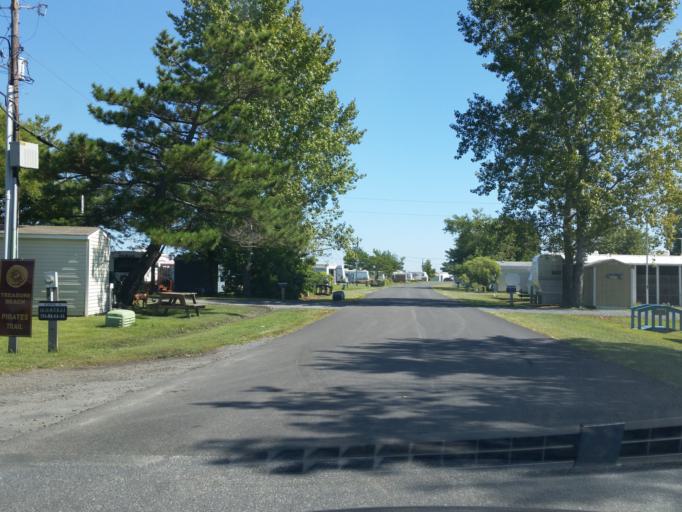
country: US
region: Delaware
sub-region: Sussex County
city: Bethany Beach
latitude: 38.4634
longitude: -75.0786
